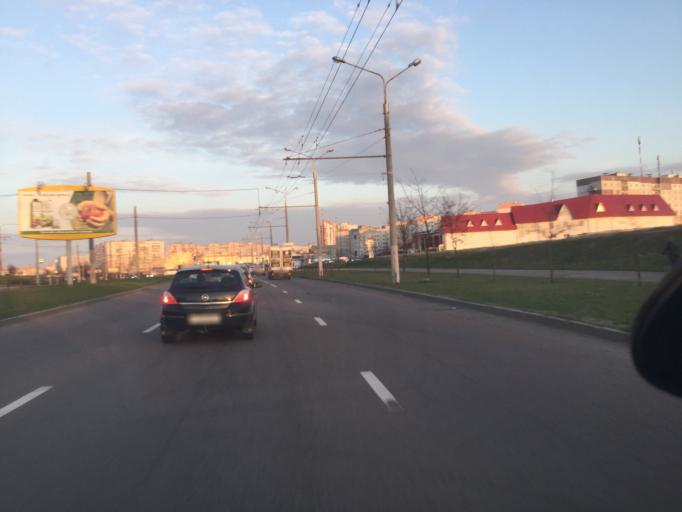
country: BY
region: Vitebsk
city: Vitebsk
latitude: 55.1655
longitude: 30.2009
